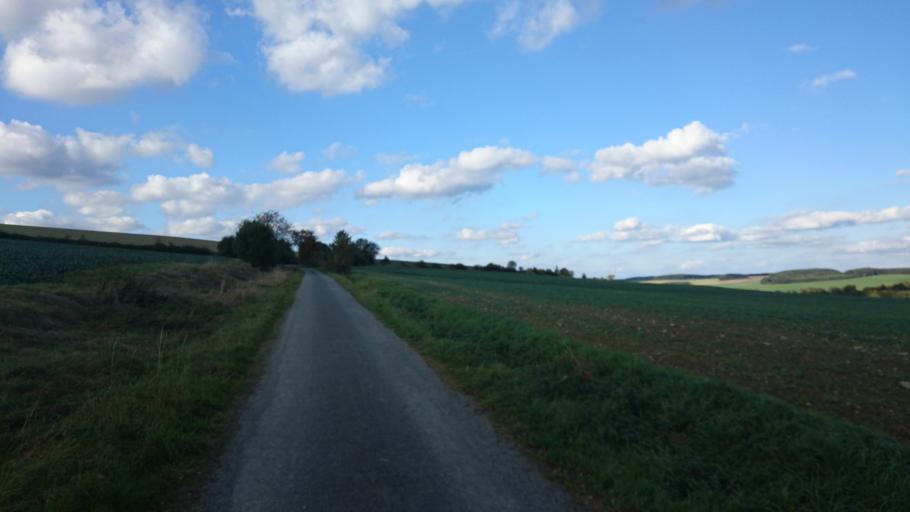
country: DE
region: Thuringia
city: Tanna
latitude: 50.4838
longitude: 11.8579
